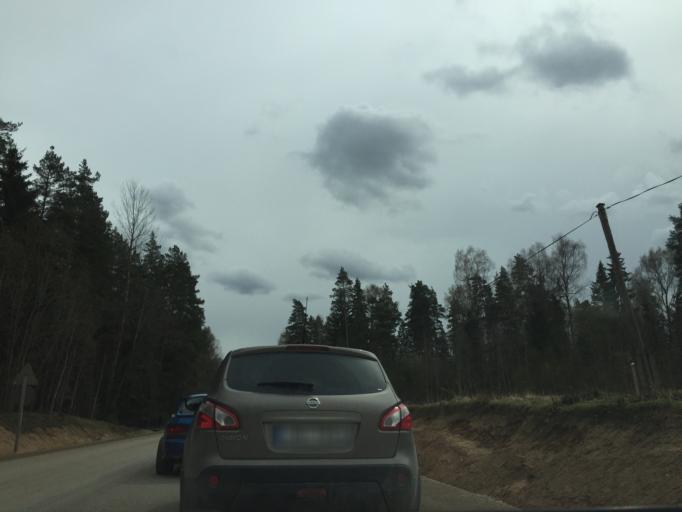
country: LV
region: Priekuli
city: Priekuli
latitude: 57.3128
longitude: 25.3796
